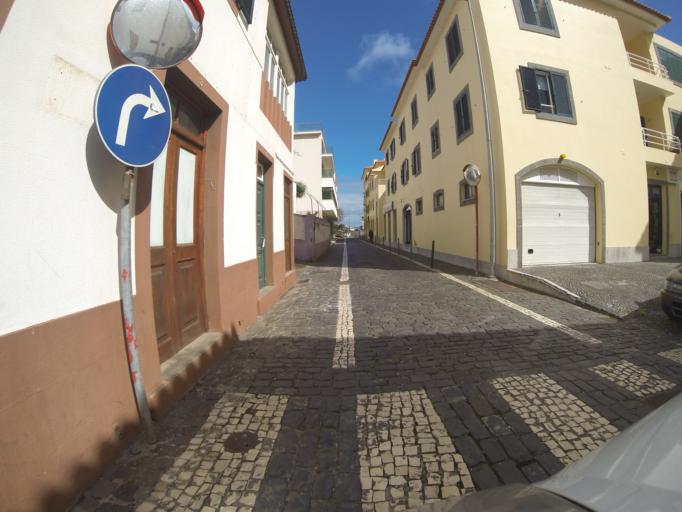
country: PT
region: Madeira
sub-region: Machico
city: Machico
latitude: 32.7186
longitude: -16.7629
